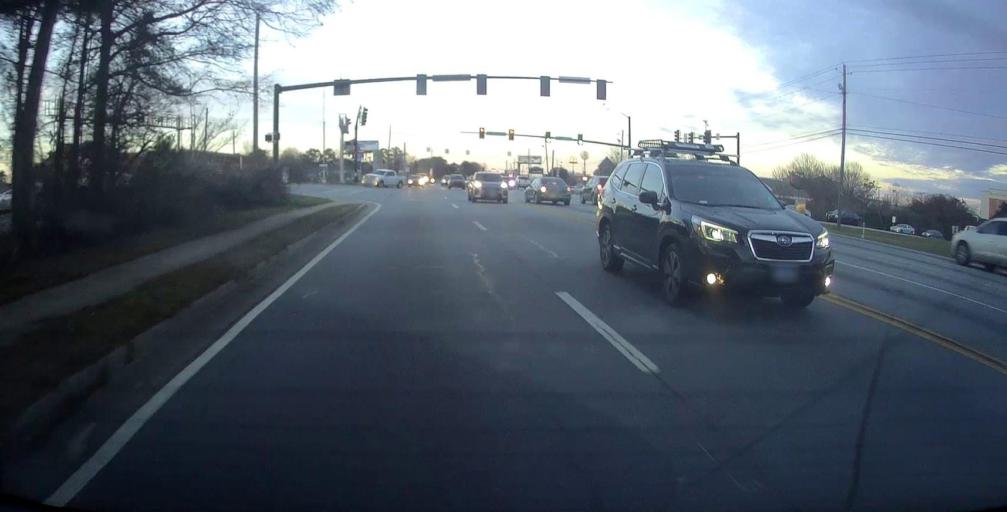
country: US
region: Alabama
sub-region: Russell County
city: Phenix City
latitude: 32.5508
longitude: -84.9498
